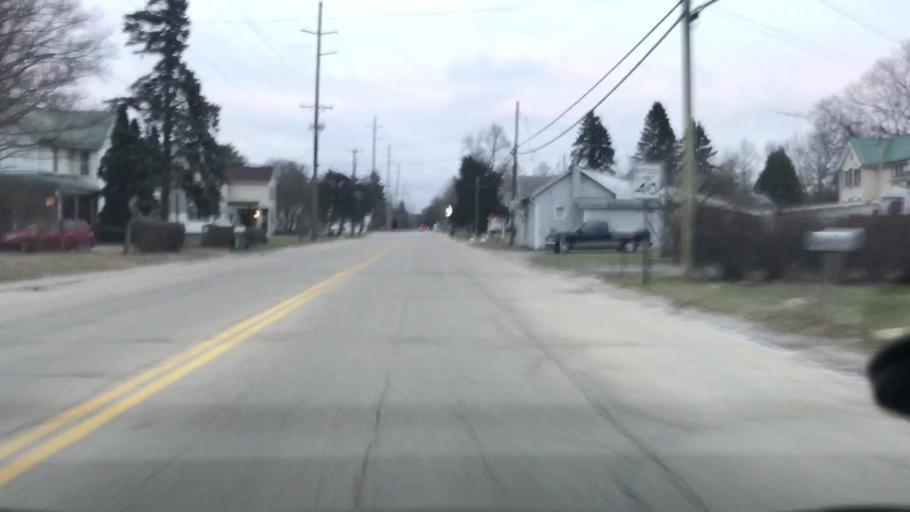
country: US
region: Ohio
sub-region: Clark County
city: Springfield
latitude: 39.9367
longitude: -83.7633
